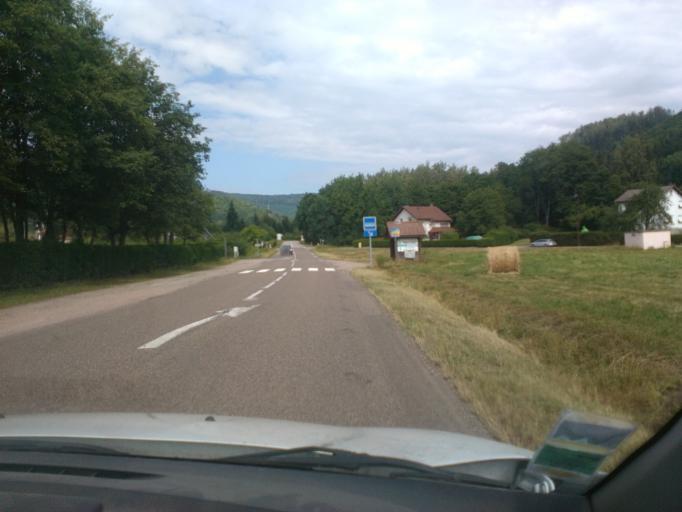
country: FR
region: Lorraine
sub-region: Departement des Vosges
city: Saulxures-sur-Moselotte
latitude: 47.9538
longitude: 6.7505
